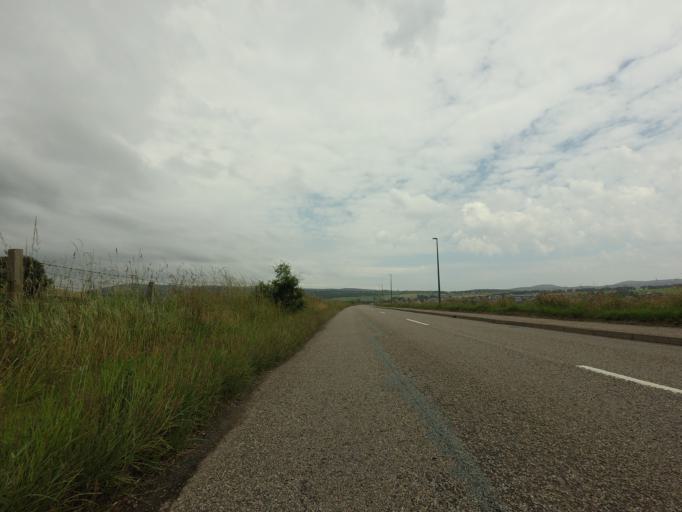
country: GB
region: Scotland
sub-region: Highland
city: Alness
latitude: 57.8843
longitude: -4.3611
